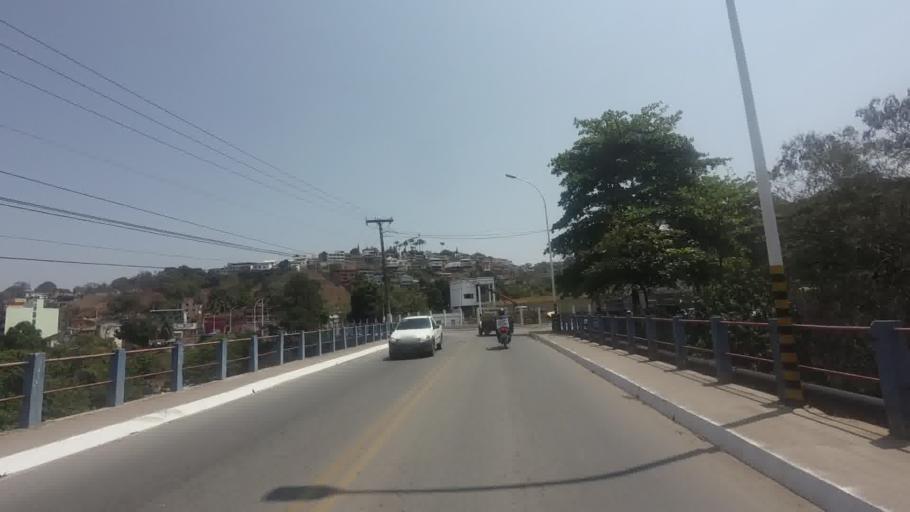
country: BR
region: Espirito Santo
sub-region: Cachoeiro De Itapemirim
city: Cachoeiro de Itapemirim
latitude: -20.8393
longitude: -41.1205
